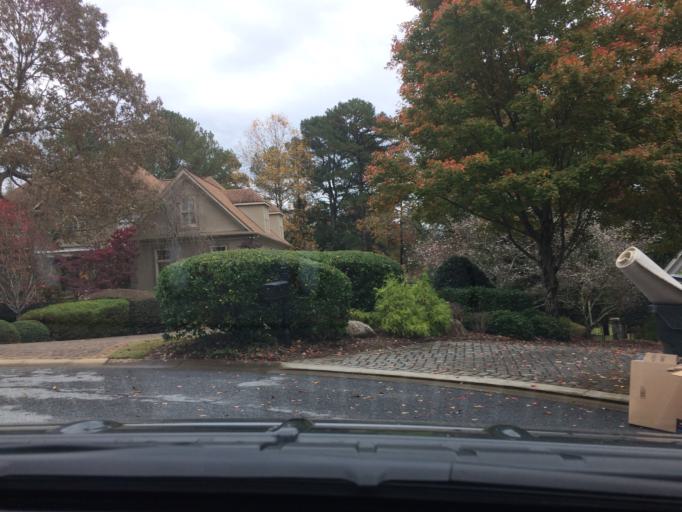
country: US
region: Georgia
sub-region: Fulton County
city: Johns Creek
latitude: 34.0083
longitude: -84.2355
